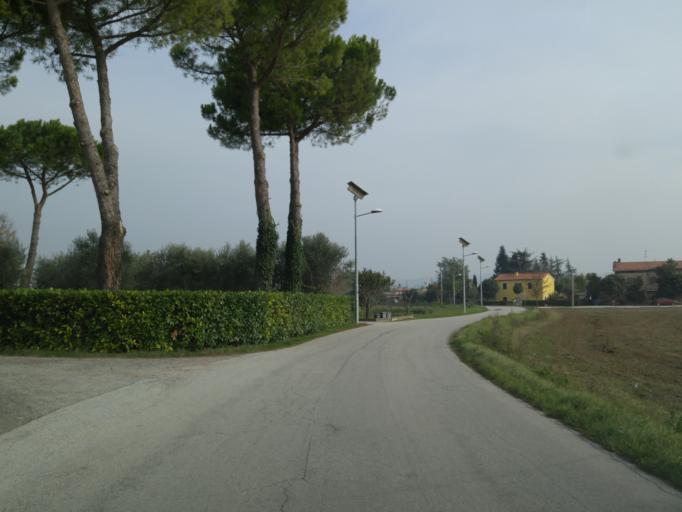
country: IT
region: The Marches
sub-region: Provincia di Pesaro e Urbino
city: Lucrezia
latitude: 43.7687
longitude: 12.9407
